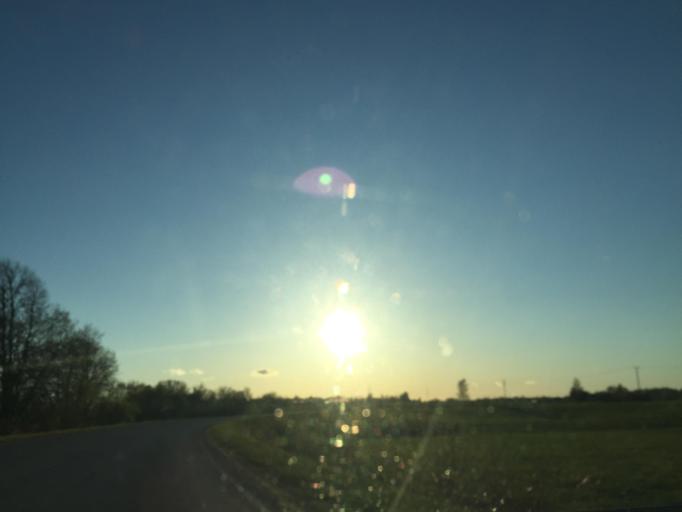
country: LV
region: Skriveri
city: Skriveri
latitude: 56.8845
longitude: 25.2189
